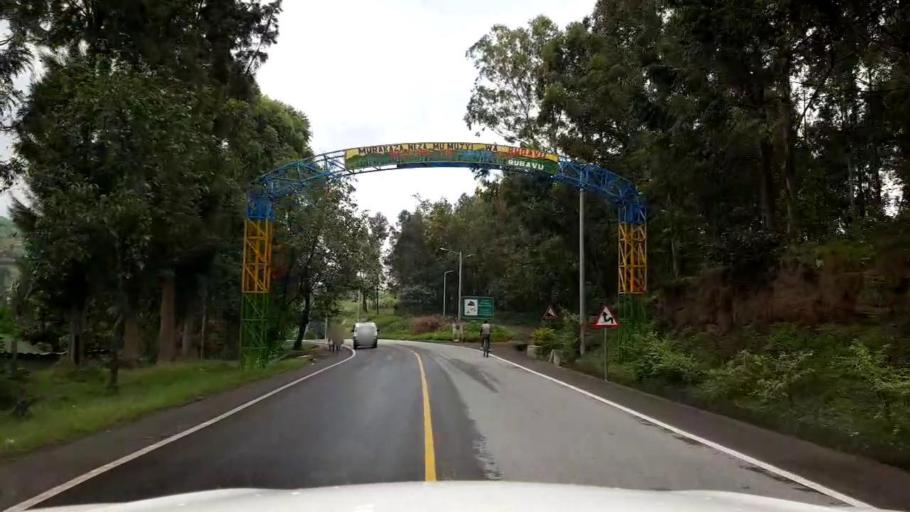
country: RW
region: Western Province
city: Gisenyi
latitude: -1.7003
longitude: 29.2714
